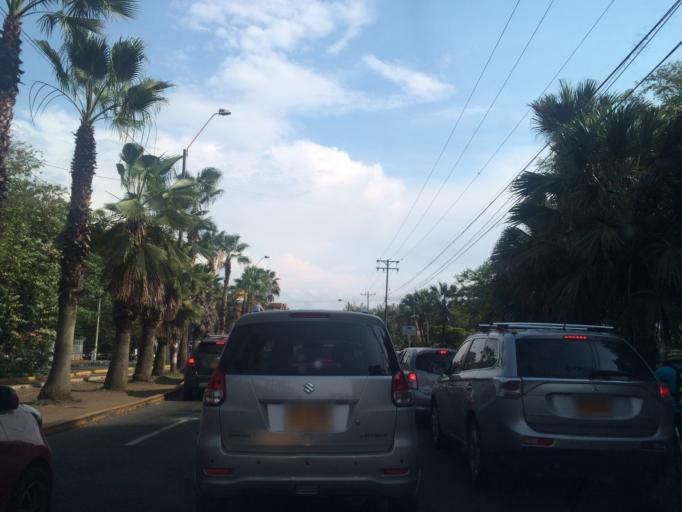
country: CO
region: Valle del Cauca
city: Cali
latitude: 3.3723
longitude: -76.5373
